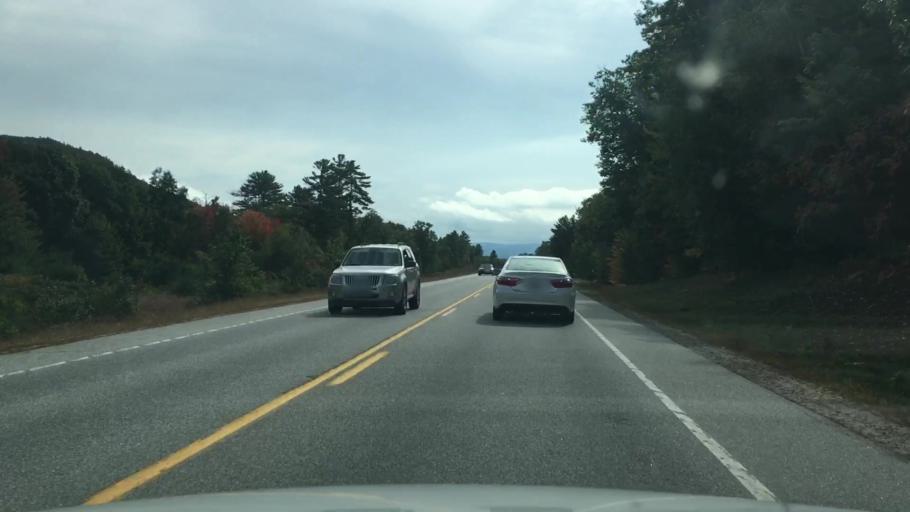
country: US
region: New Hampshire
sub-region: Carroll County
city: North Conway
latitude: 44.0329
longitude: -71.1149
